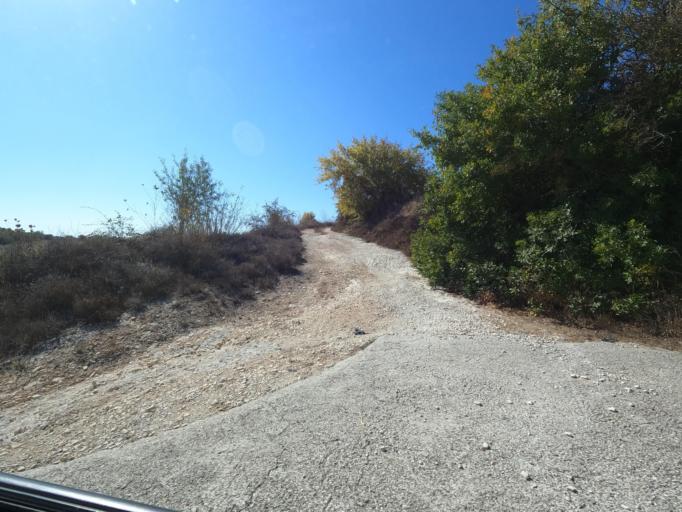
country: CY
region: Pafos
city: Mesogi
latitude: 34.8042
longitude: 32.4864
